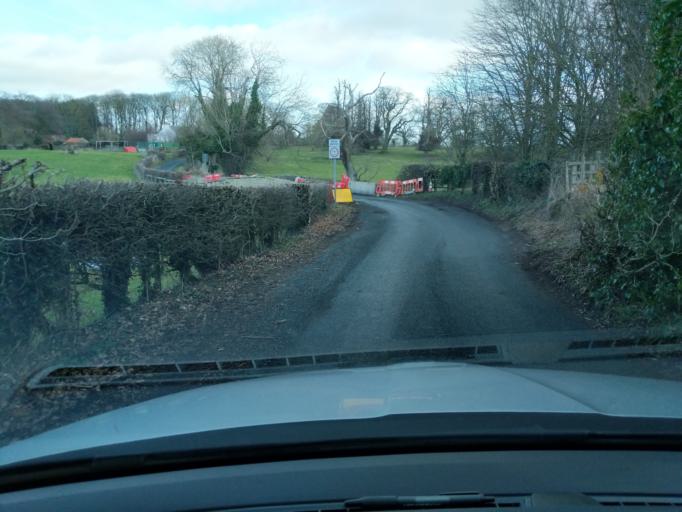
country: GB
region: England
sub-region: North Yorkshire
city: Catterick
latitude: 54.3762
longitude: -1.6726
